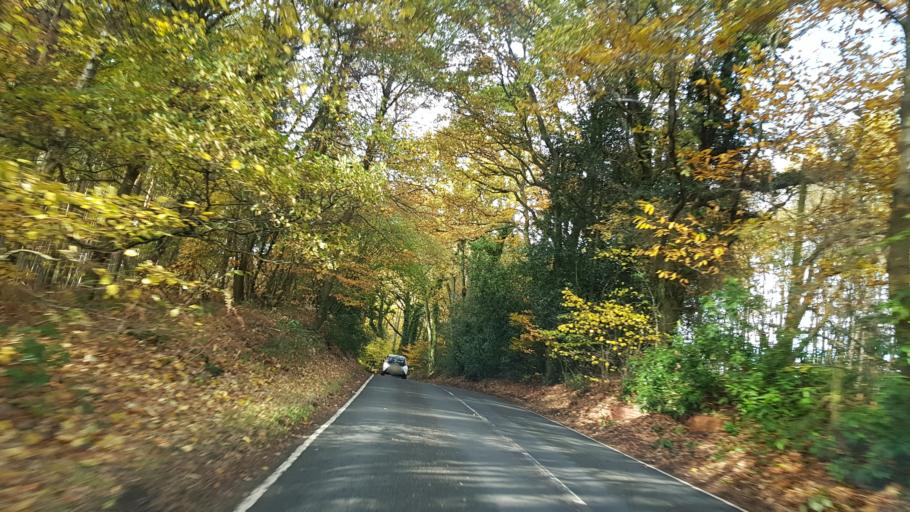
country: GB
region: England
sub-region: Surrey
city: Seale
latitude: 51.1996
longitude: -0.7457
